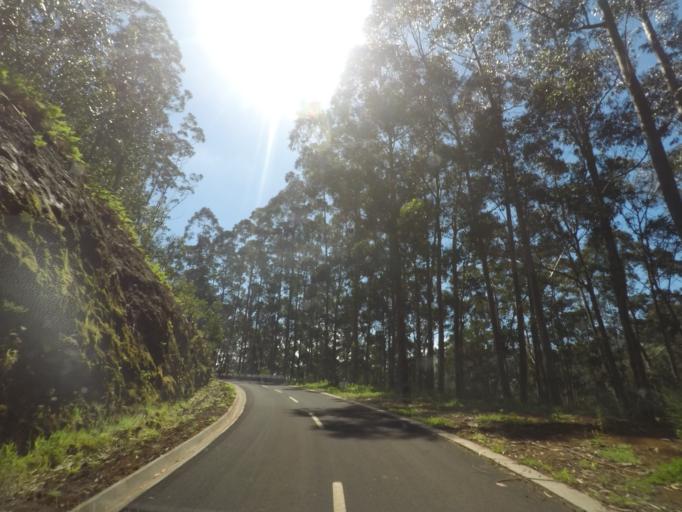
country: PT
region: Madeira
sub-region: Calheta
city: Arco da Calheta
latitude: 32.7265
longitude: -17.1226
